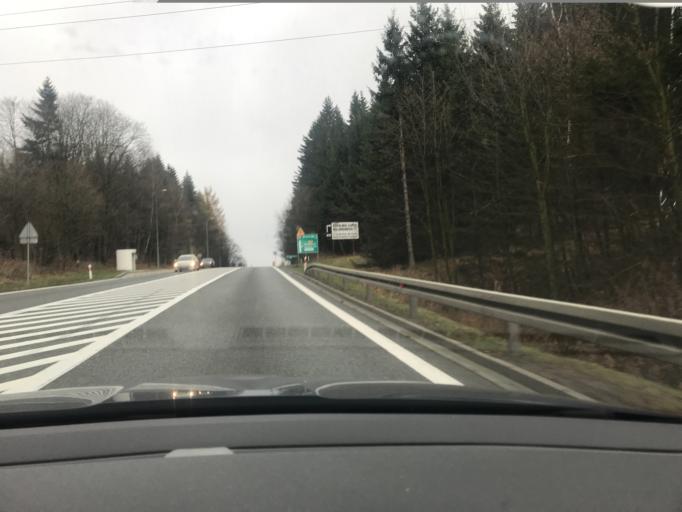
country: PL
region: Lower Silesian Voivodeship
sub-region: Powiat klodzki
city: Duszniki-Zdroj
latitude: 50.3985
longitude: 16.3477
